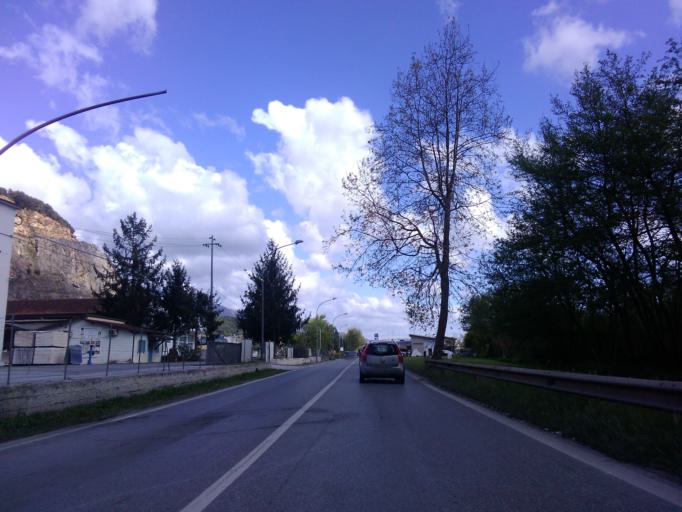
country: IT
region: Tuscany
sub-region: Provincia di Massa-Carrara
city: Capanne-Prato-Cinquale
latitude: 43.9961
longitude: 10.1745
